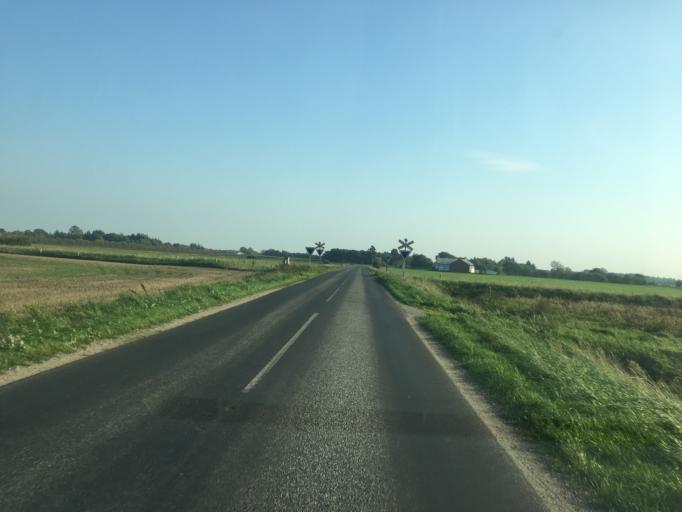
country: DE
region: Schleswig-Holstein
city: Bramstedtlund
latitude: 54.9432
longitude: 9.0637
